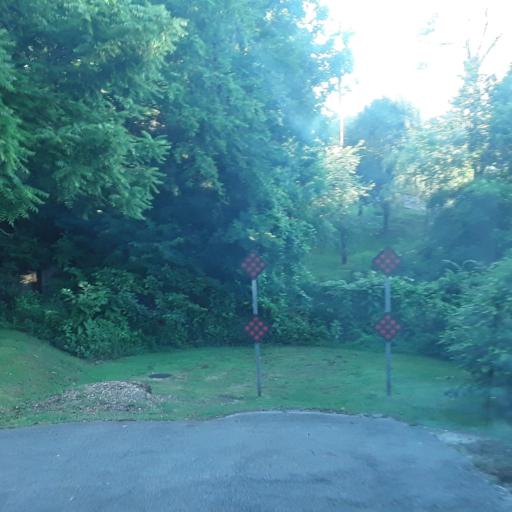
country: US
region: Tennessee
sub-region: Davidson County
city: Oak Hill
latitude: 36.1055
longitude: -86.7332
